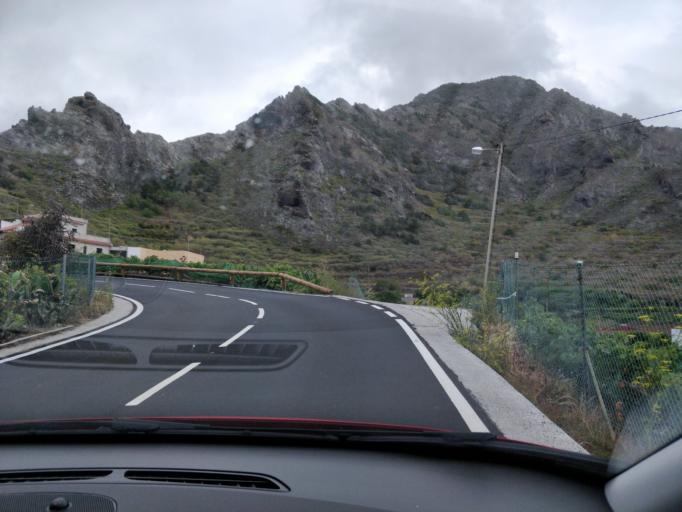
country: ES
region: Canary Islands
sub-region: Provincia de Santa Cruz de Tenerife
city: Tanque
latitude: 28.3495
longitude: -16.8455
